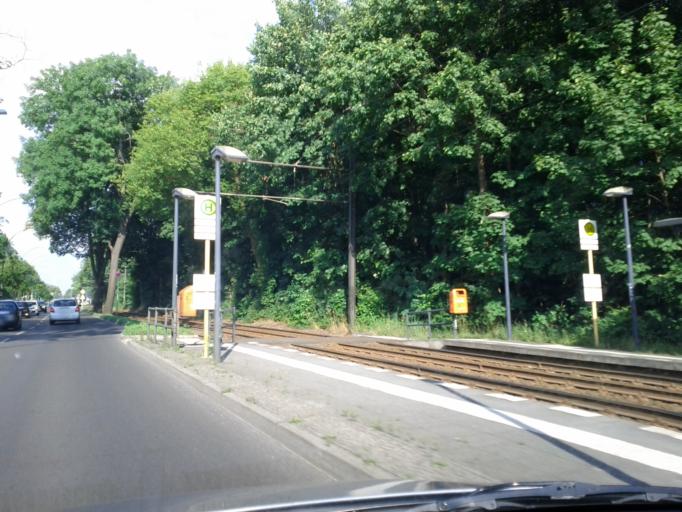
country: DE
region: Berlin
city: Friedrichshagen
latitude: 52.4543
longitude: 13.6131
